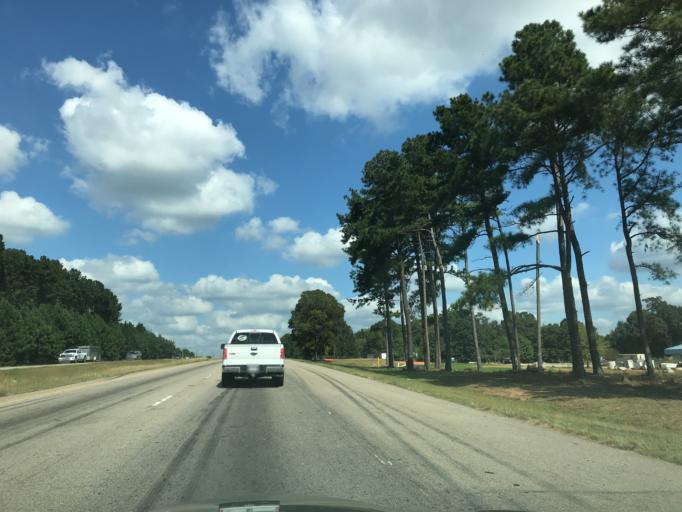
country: US
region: North Carolina
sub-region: Wake County
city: Wake Forest
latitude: 35.9146
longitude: -78.5498
